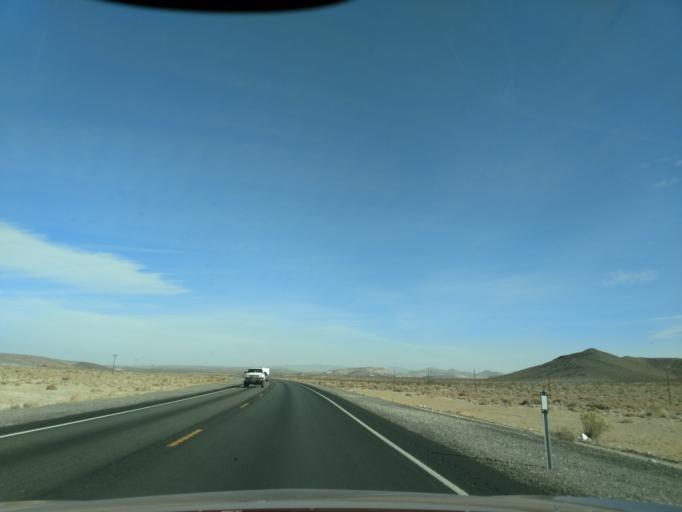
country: US
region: Nevada
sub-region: Nye County
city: Beatty
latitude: 36.9240
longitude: -116.7404
